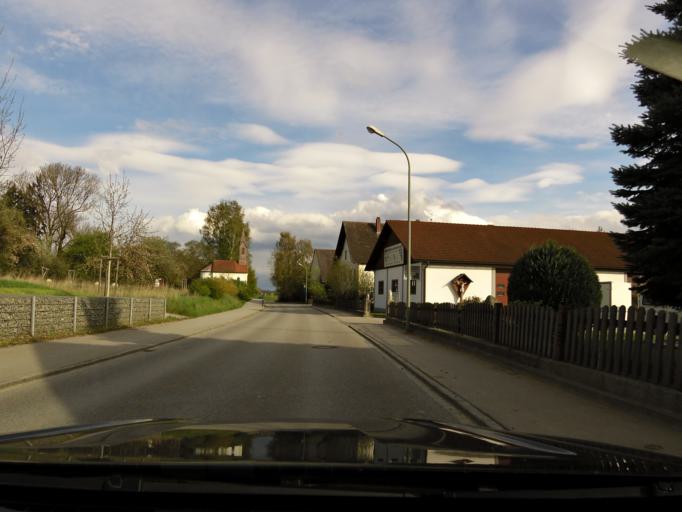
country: DE
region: Bavaria
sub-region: Upper Bavaria
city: Mauern
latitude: 48.5075
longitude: 11.9123
